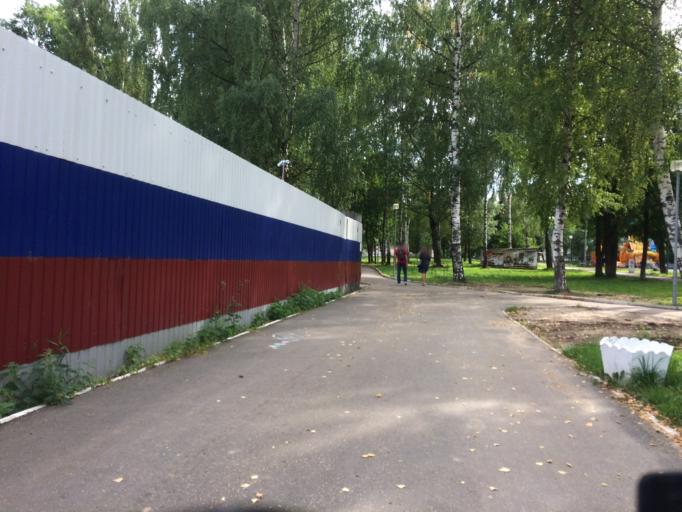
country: RU
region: Mariy-El
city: Yoshkar-Ola
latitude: 56.6400
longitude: 47.8677
